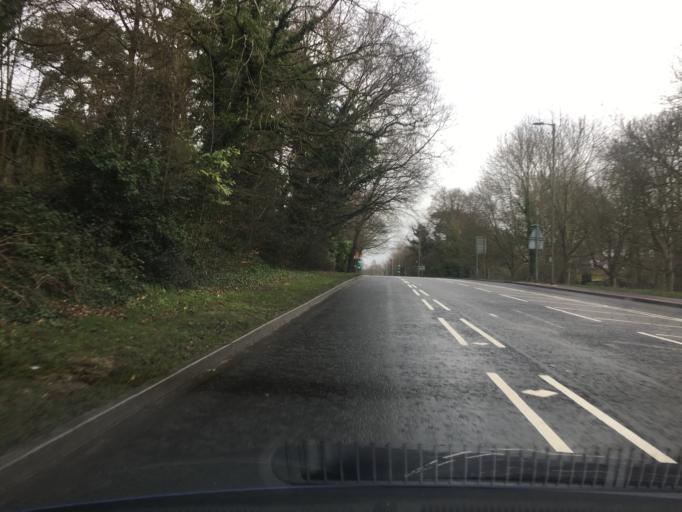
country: GB
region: England
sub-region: Bracknell Forest
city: Bracknell
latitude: 51.4108
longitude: -0.7551
